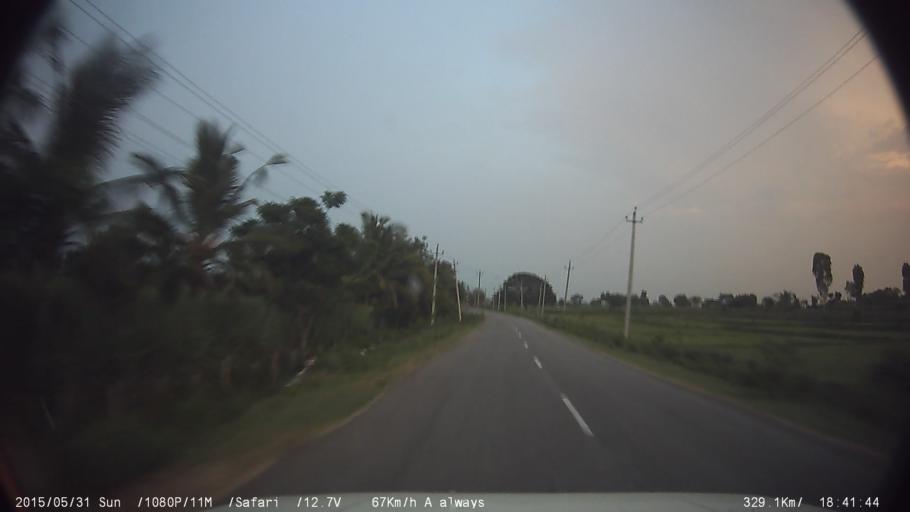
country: IN
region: Karnataka
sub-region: Mysore
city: Nanjangud
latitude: 12.1505
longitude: 76.7953
